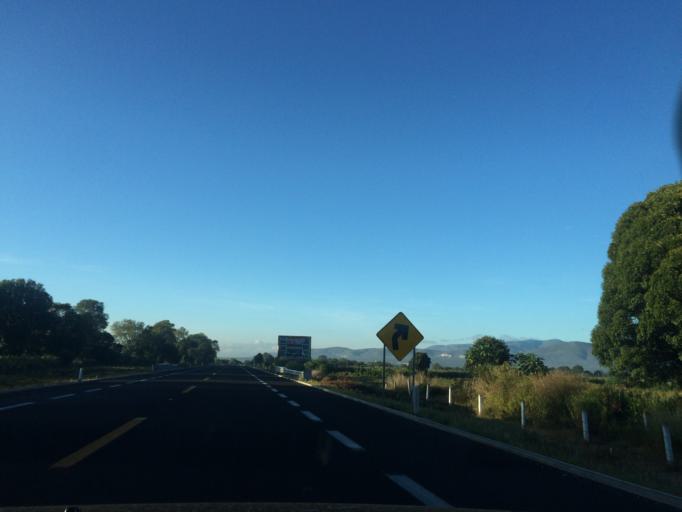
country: MX
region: Puebla
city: Santiago Miahuatlan
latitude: 18.5285
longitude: -97.4564
